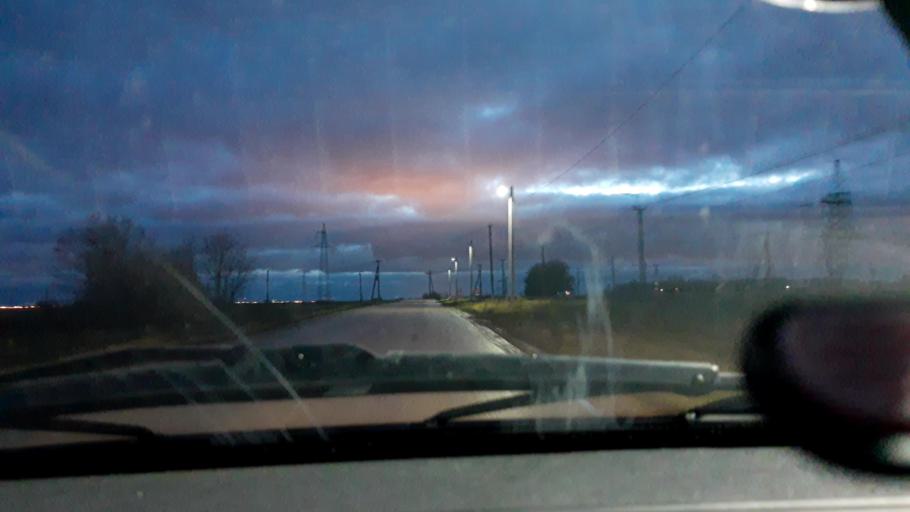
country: RU
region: Bashkortostan
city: Mikhaylovka
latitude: 54.8294
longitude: 55.8818
